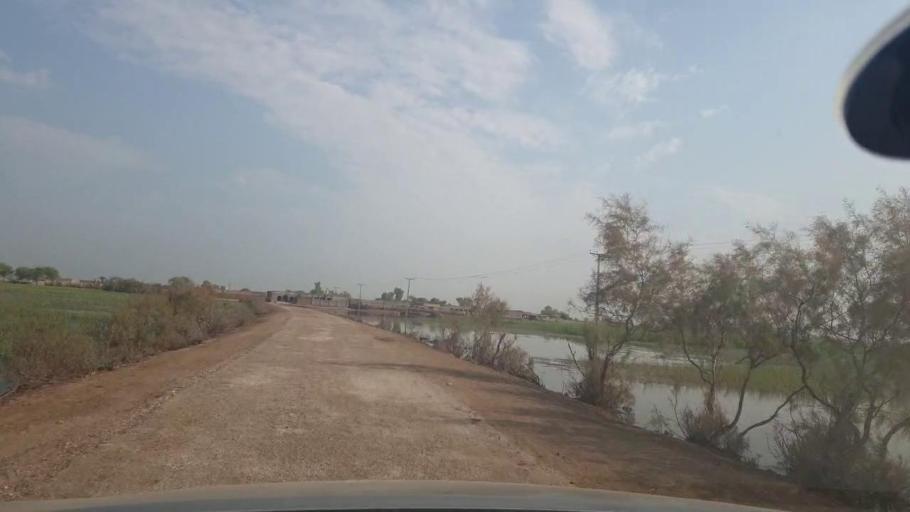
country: PK
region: Balochistan
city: Mehrabpur
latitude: 28.0714
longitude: 68.2109
